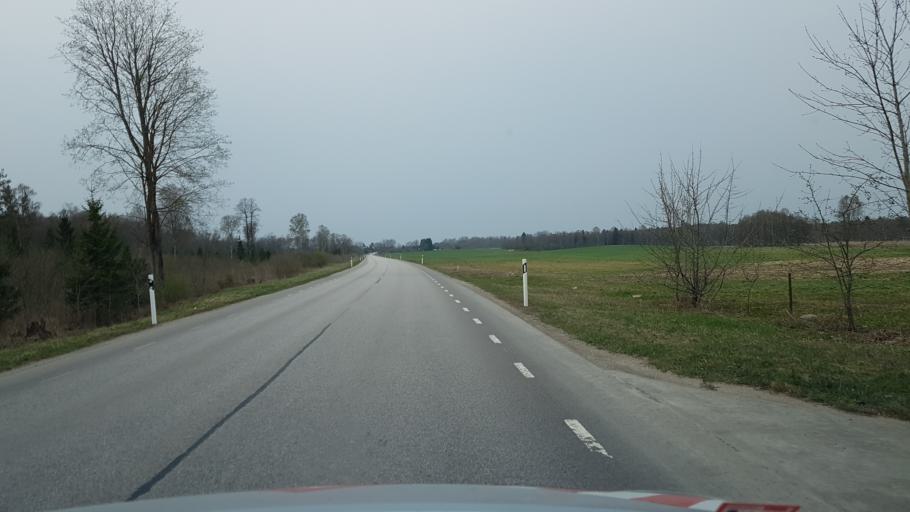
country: EE
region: Harju
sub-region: Raasiku vald
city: Arukula
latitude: 59.3731
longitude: 25.0241
